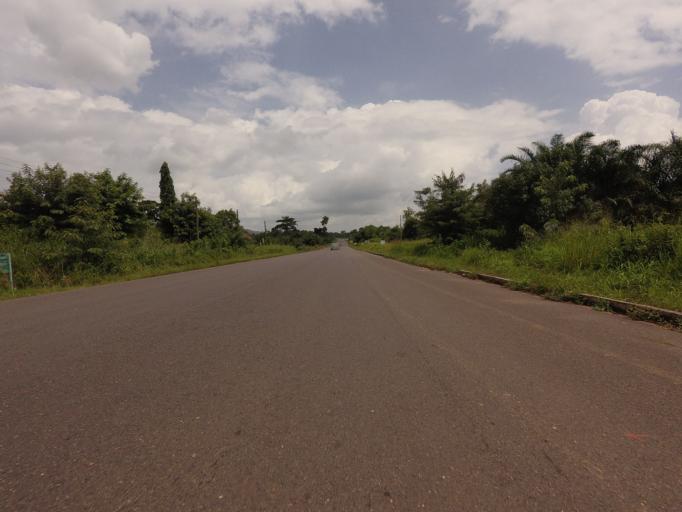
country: GH
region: Volta
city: Ho
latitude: 6.5267
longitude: 0.2242
